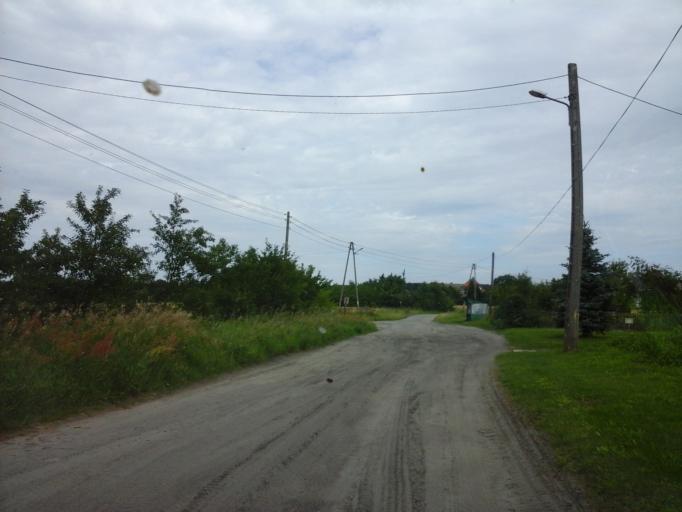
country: PL
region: Lubusz
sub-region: Powiat strzelecko-drezdenecki
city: Dobiegniew
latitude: 53.0482
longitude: 15.7596
